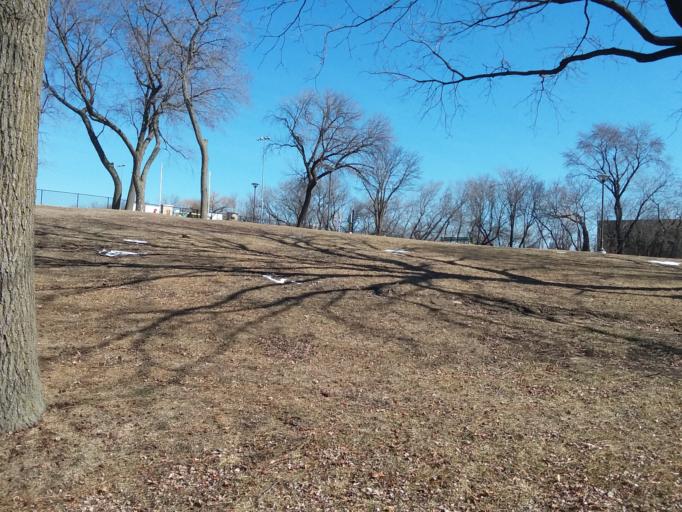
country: US
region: Wisconsin
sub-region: Milwaukee County
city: West Milwaukee
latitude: 43.0249
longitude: -87.9412
